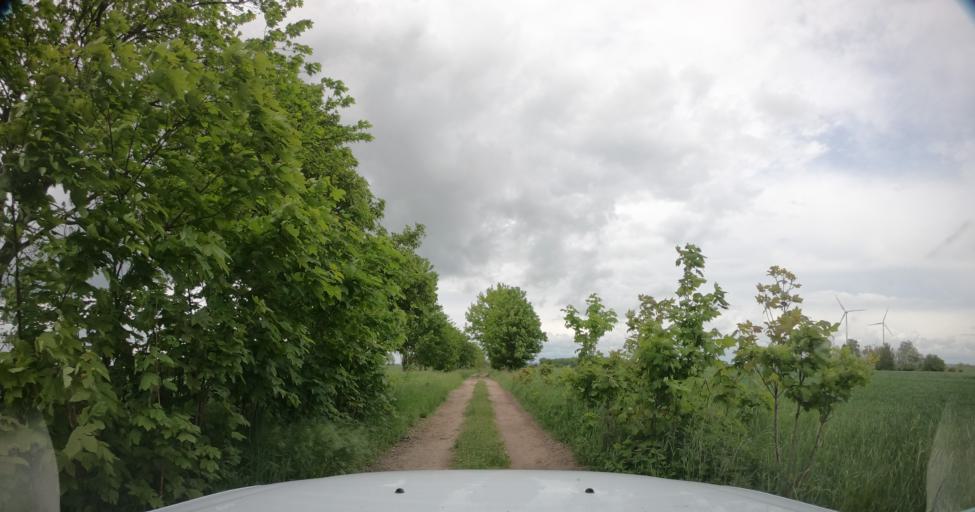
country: PL
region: West Pomeranian Voivodeship
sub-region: Powiat pyrzycki
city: Kozielice
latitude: 53.0869
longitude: 14.8242
